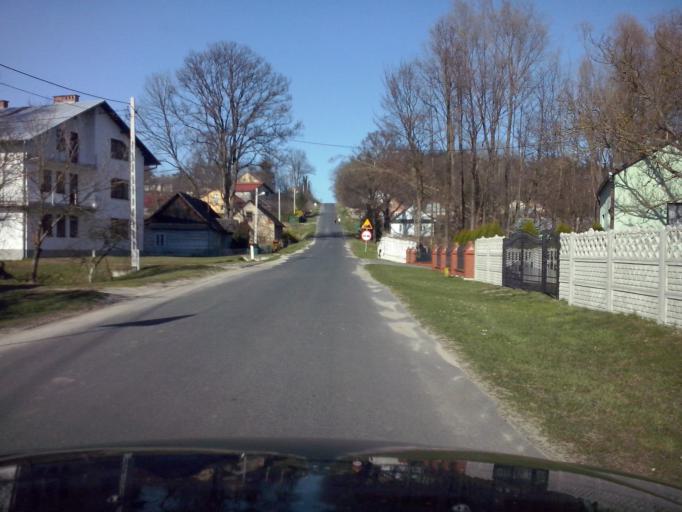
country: PL
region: Subcarpathian Voivodeship
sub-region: Powiat nizanski
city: Krzeszow
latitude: 50.3883
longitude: 22.3772
